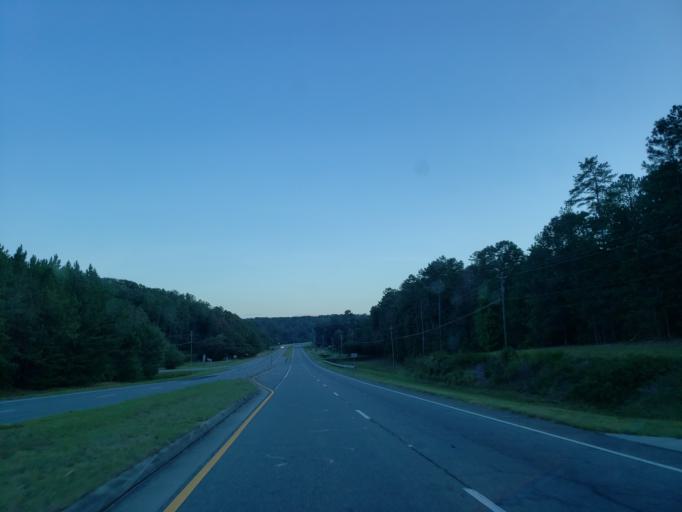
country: US
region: Georgia
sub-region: Floyd County
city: Lindale
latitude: 34.1353
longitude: -85.2161
